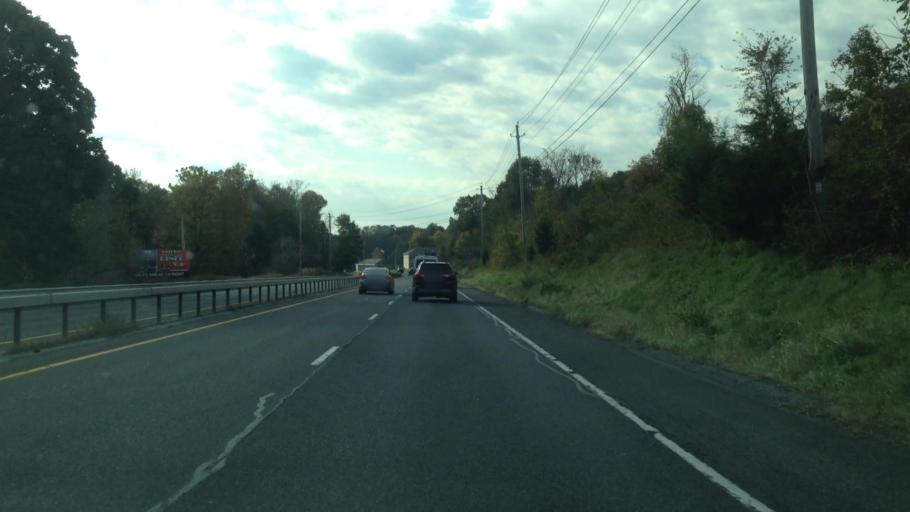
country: US
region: New York
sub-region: Ulster County
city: Highland
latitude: 41.7323
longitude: -73.9615
